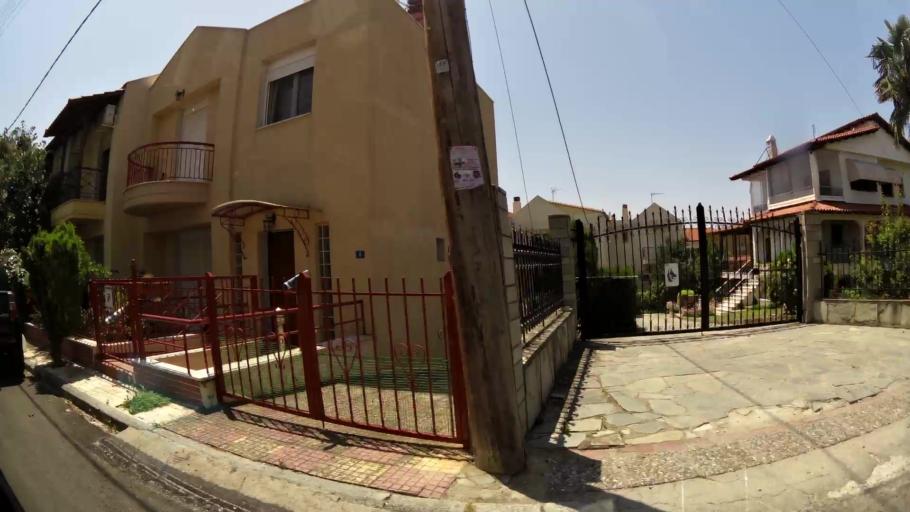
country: GR
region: Central Macedonia
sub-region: Nomos Thessalonikis
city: Trilofos
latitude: 40.4665
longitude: 22.9750
